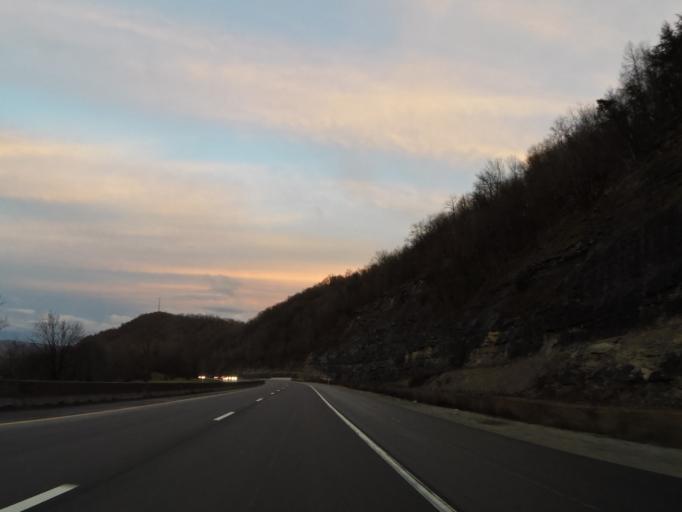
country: US
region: Tennessee
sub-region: Campbell County
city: Jellico
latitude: 36.5511
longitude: -84.1433
